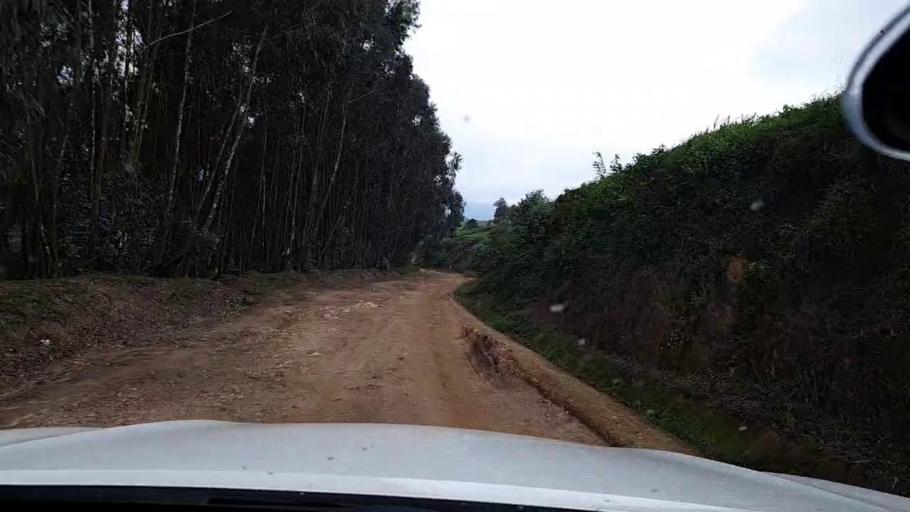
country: RW
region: Western Province
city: Kibuye
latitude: -2.2492
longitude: 29.3453
